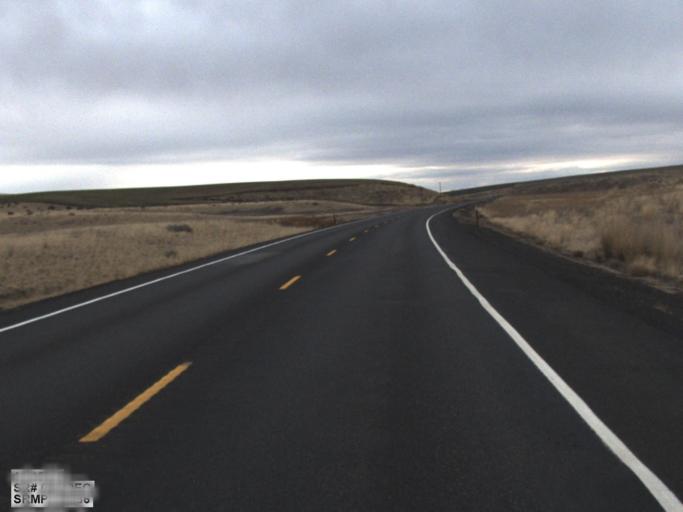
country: US
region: Washington
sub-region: Garfield County
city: Pomeroy
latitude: 46.7990
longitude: -117.8531
